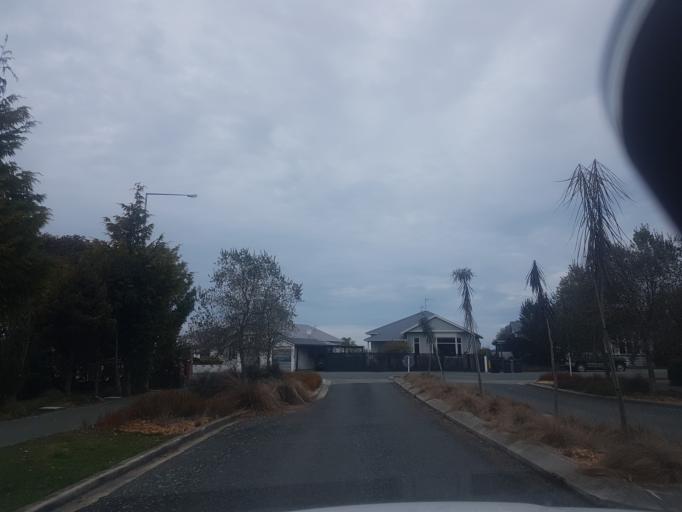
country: NZ
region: Canterbury
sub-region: Timaru District
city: Timaru
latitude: -44.4043
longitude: 171.2350
